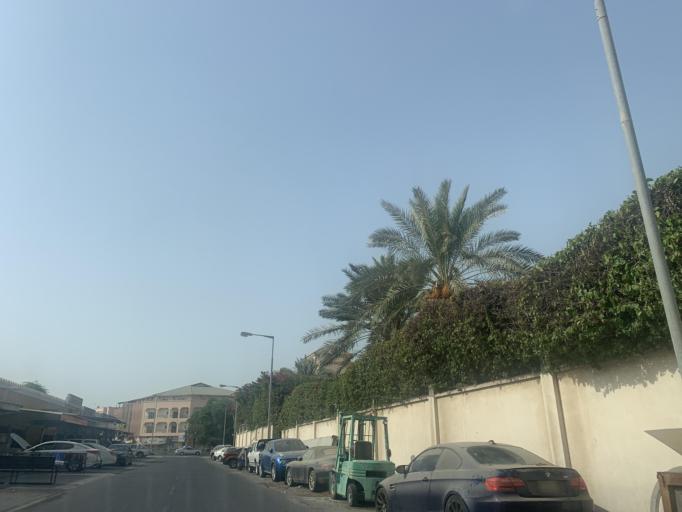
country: BH
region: Manama
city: Jidd Hafs
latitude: 26.2152
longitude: 50.4737
